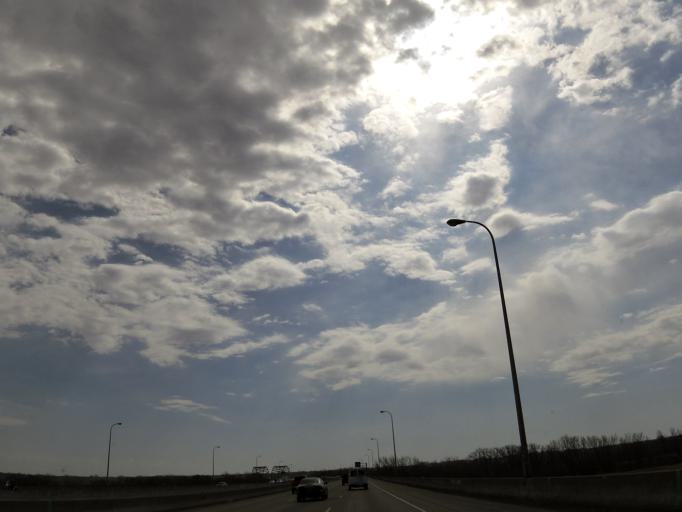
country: US
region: Minnesota
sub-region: Hennepin County
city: Bloomington
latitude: 44.8335
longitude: -93.2385
